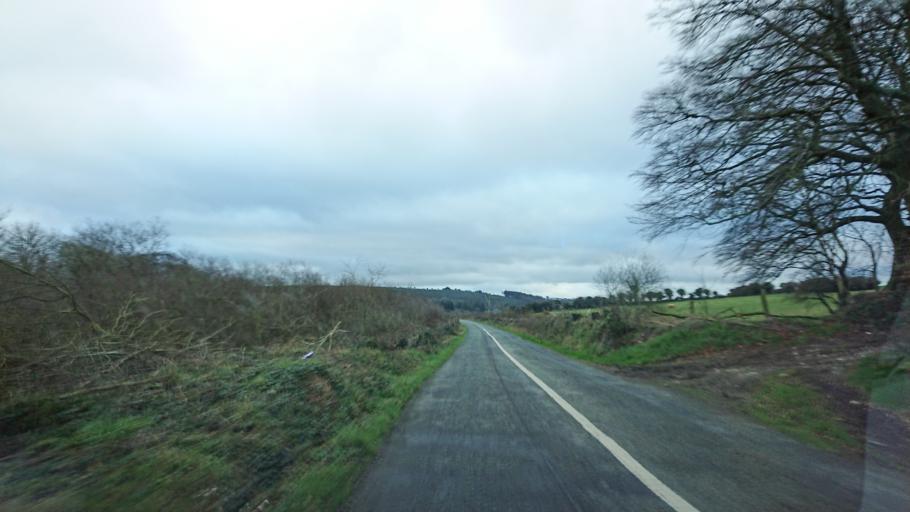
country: IE
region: Munster
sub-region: Waterford
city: Portlaw
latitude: 52.2346
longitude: -7.4112
